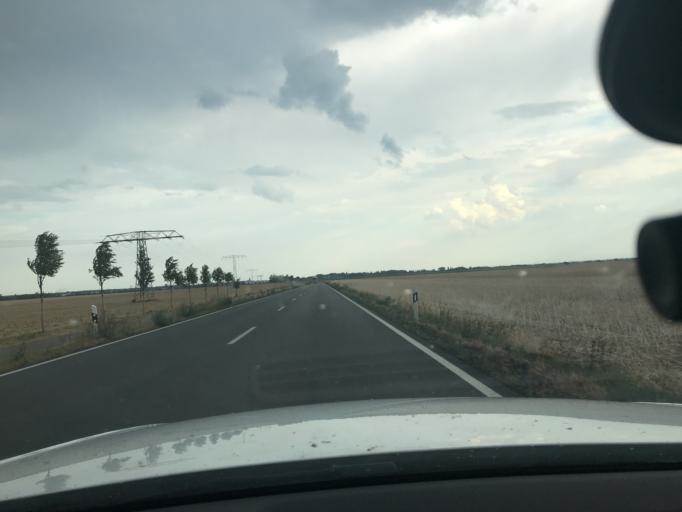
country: DE
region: Saxony
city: Markranstadt
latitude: 51.3282
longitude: 12.2065
